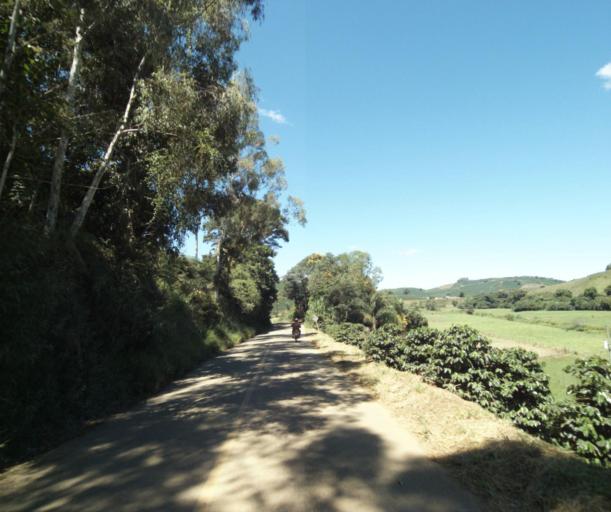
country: BR
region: Minas Gerais
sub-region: Espera Feliz
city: Espera Feliz
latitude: -20.5949
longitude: -41.8391
